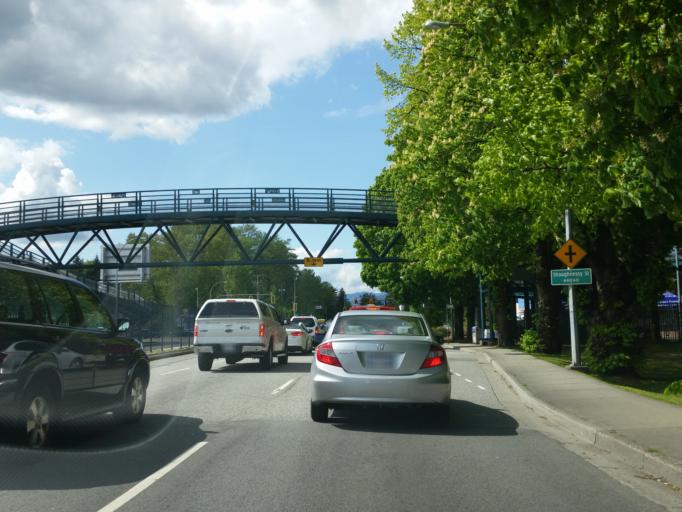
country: CA
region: British Columbia
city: Coquitlam
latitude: 49.2669
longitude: -122.7748
